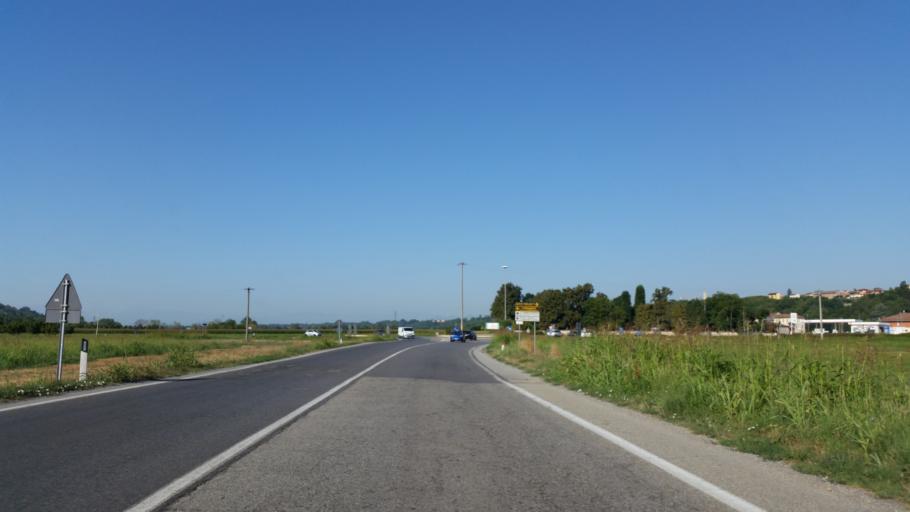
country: IT
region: Piedmont
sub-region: Provincia di Cuneo
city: Roreto
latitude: 44.6670
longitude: 7.8563
